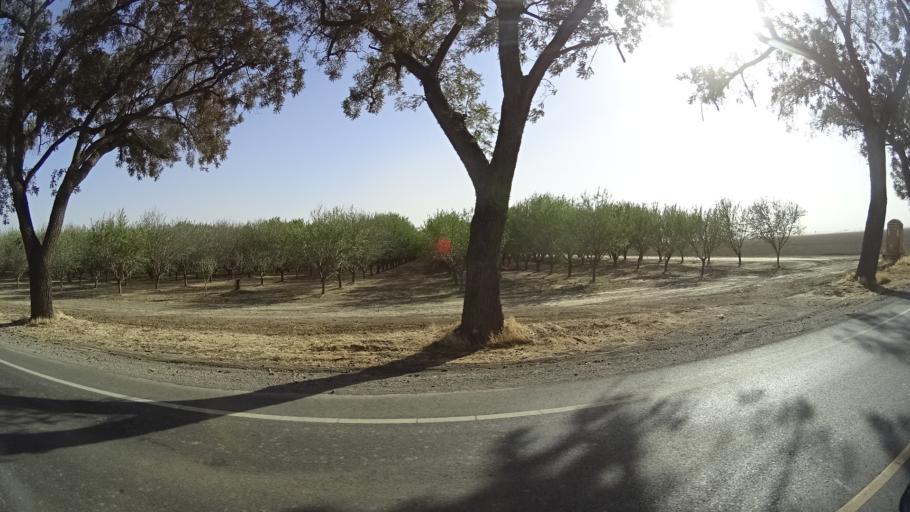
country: US
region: California
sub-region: Yolo County
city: Woodland
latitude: 38.7928
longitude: -121.7462
